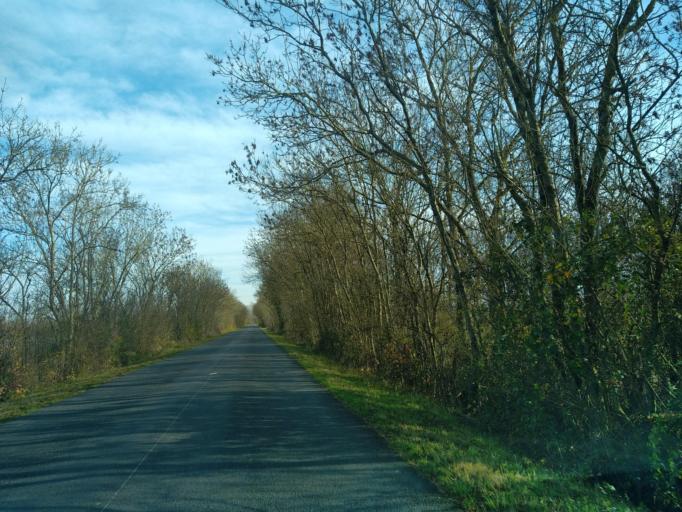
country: FR
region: Pays de la Loire
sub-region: Departement de la Vendee
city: Maillezais
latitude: 46.3785
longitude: -0.7664
